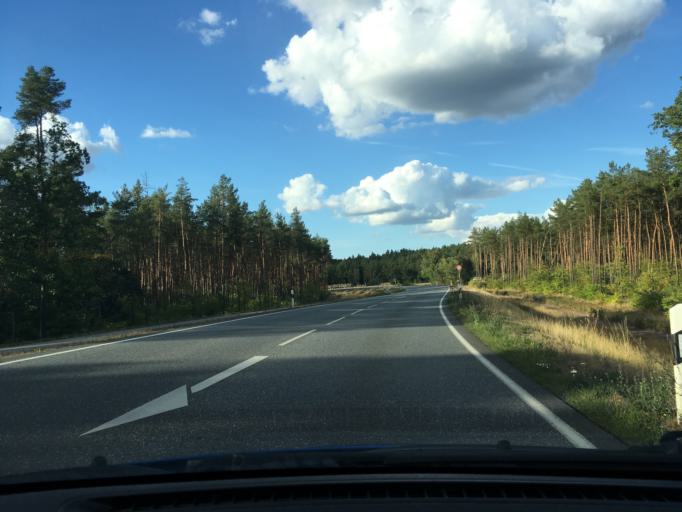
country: DE
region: Mecklenburg-Vorpommern
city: Ludwigslust
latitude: 53.3008
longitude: 11.5238
